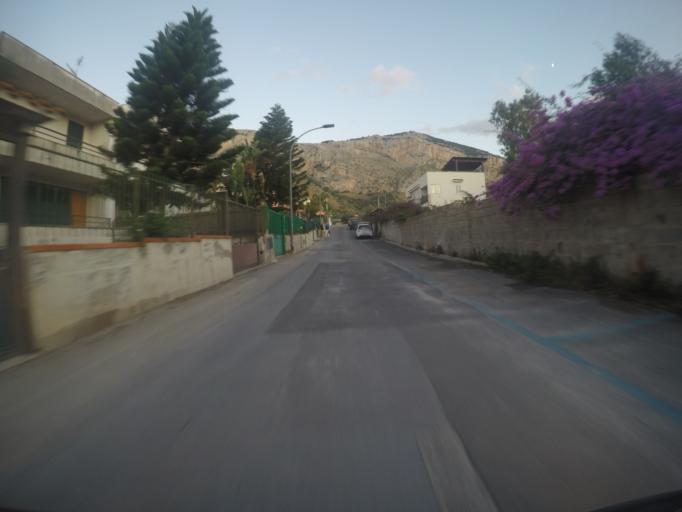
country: IT
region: Sicily
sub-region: Palermo
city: Isola delle Femmine
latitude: 38.1845
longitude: 13.2415
